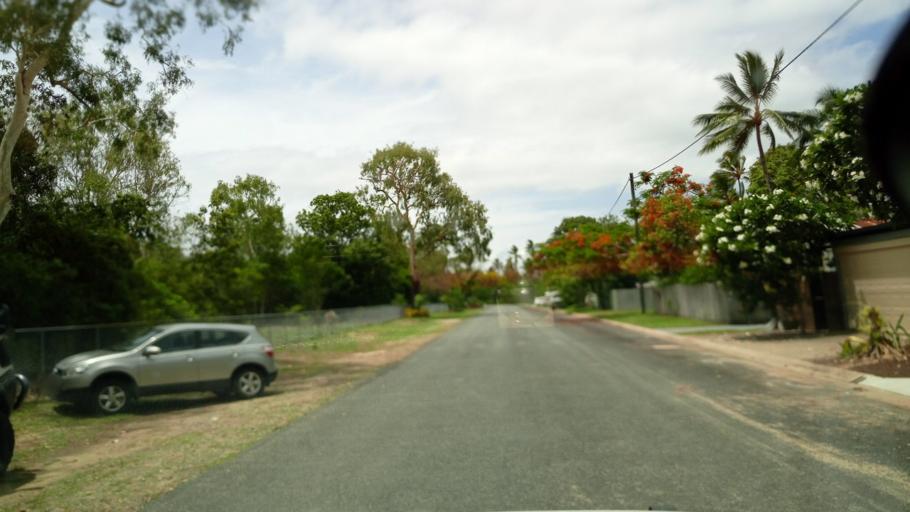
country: AU
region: Queensland
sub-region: Cairns
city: Redlynch
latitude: -16.8579
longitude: 145.7555
